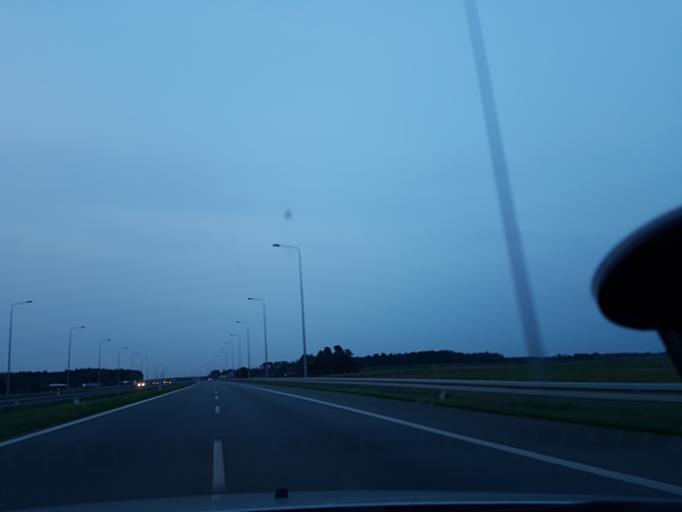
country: PL
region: Lodz Voivodeship
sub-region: Powiat leczycki
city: Piatek
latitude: 52.0122
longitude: 19.5422
